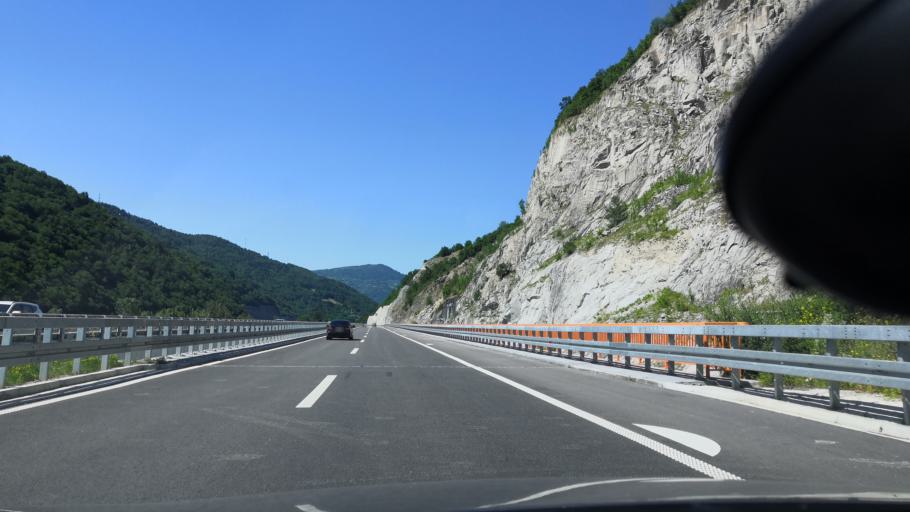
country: RS
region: Central Serbia
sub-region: Pcinjski Okrug
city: Vladicin Han
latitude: 42.7582
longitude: 22.0856
